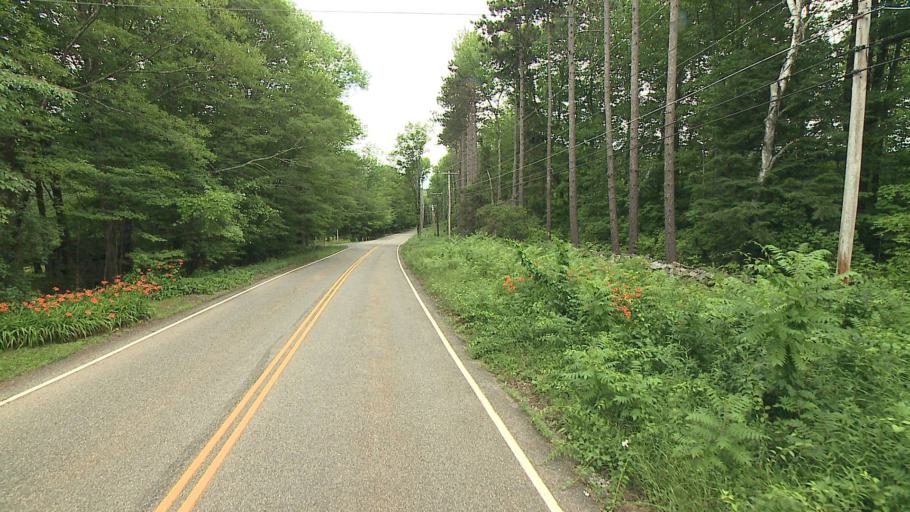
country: US
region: Connecticut
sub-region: Litchfield County
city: Winsted
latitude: 42.0011
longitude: -73.0024
